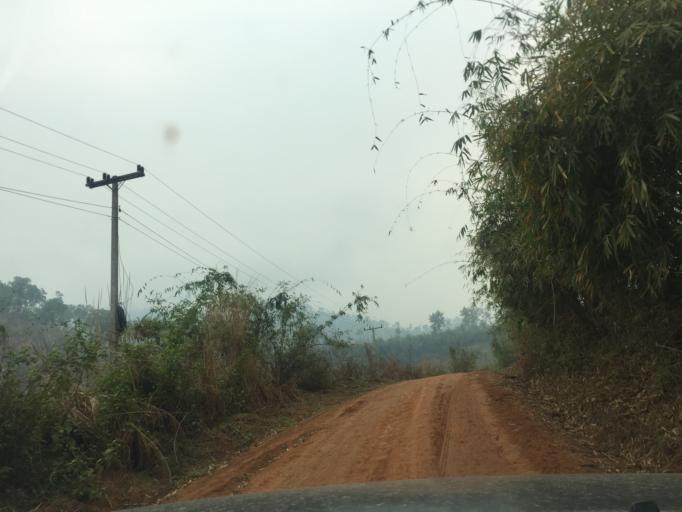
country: TH
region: Nan
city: Bo Kluea
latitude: 18.8497
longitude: 101.4176
